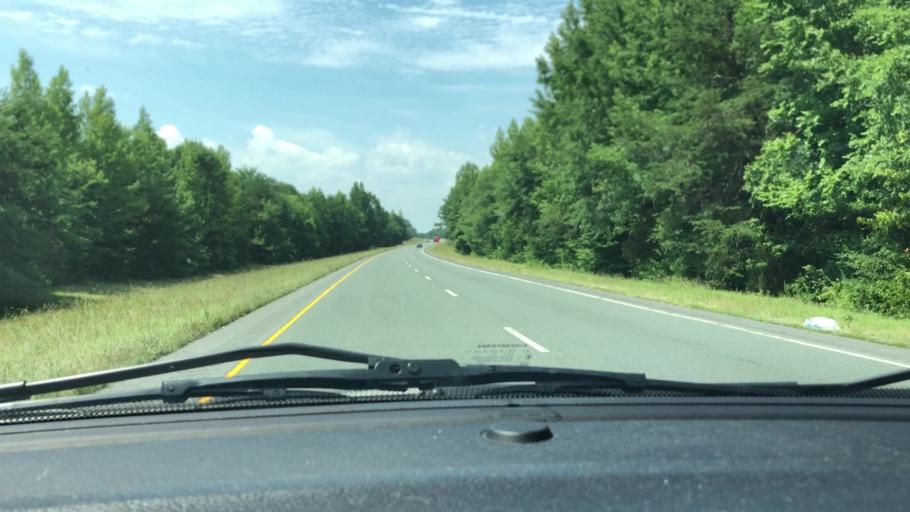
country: US
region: North Carolina
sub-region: Randolph County
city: Liberty
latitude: 35.8693
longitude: -79.6284
